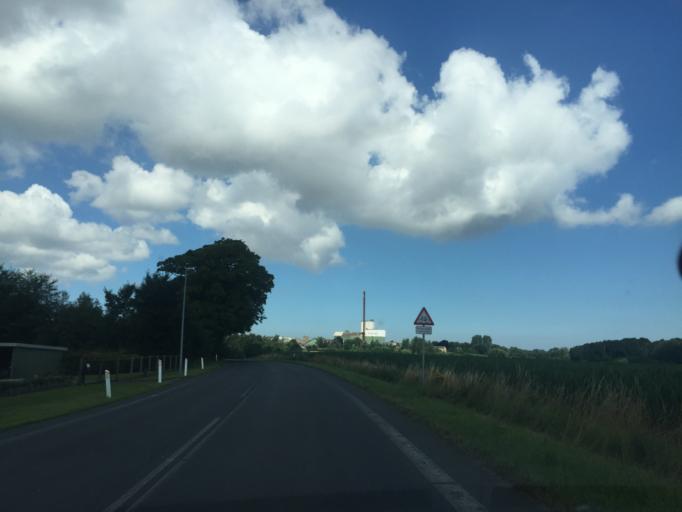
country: DK
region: South Denmark
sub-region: Nordfyns Kommune
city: Otterup
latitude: 55.5302
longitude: 10.3894
